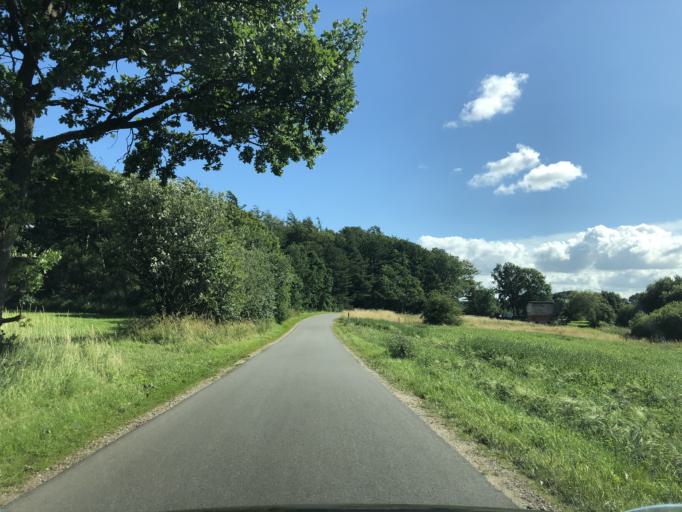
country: DK
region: Central Jutland
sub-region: Viborg Kommune
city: Stoholm
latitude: 56.4403
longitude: 9.1314
